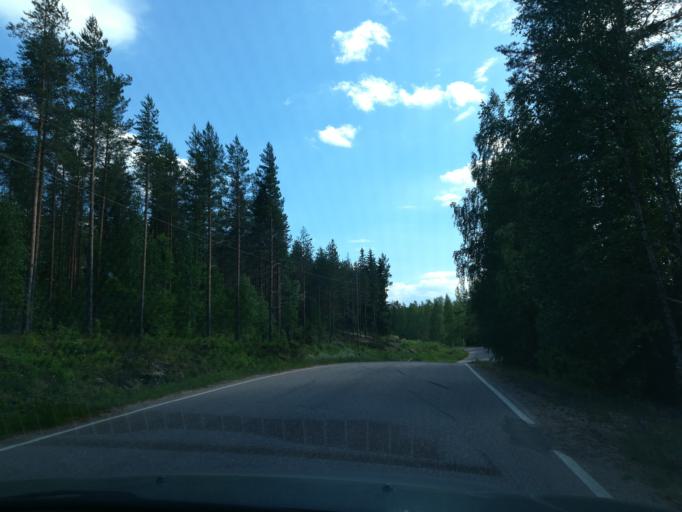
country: FI
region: South Karelia
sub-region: Imatra
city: Ruokolahti
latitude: 61.4840
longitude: 28.7860
